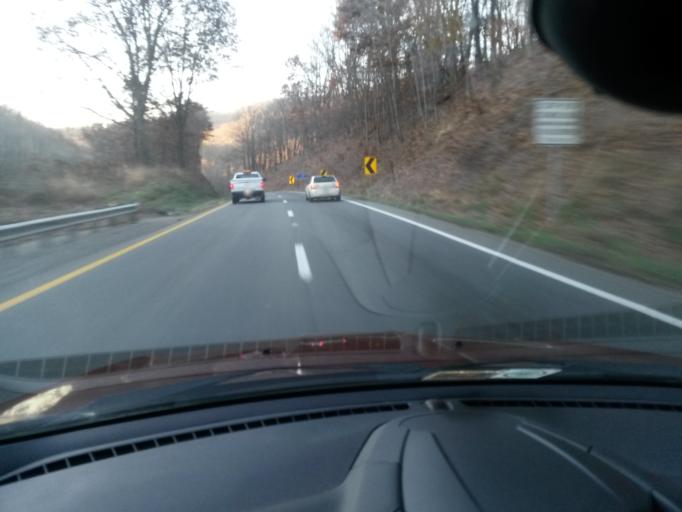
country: US
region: Virginia
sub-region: Roanoke County
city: Narrows
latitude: 37.1393
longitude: -79.9729
